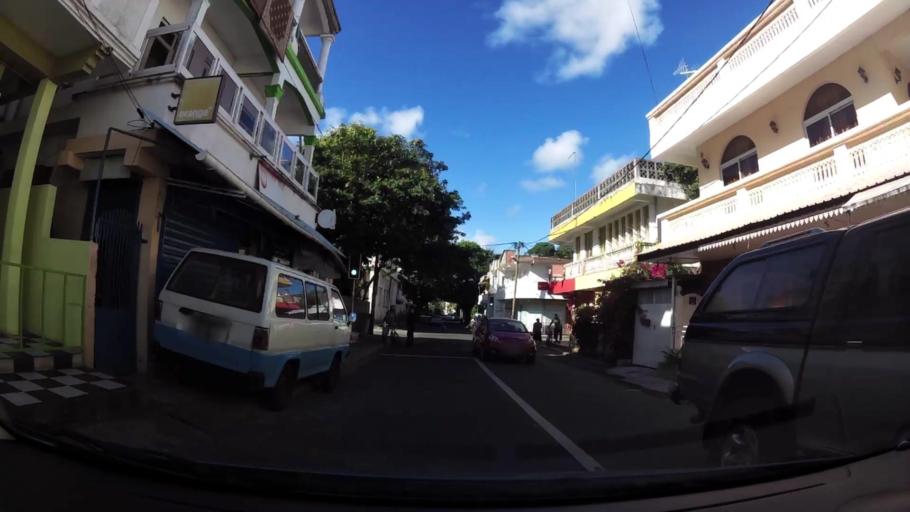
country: MU
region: Grand Port
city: Mahebourg
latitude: -20.4101
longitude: 57.7095
